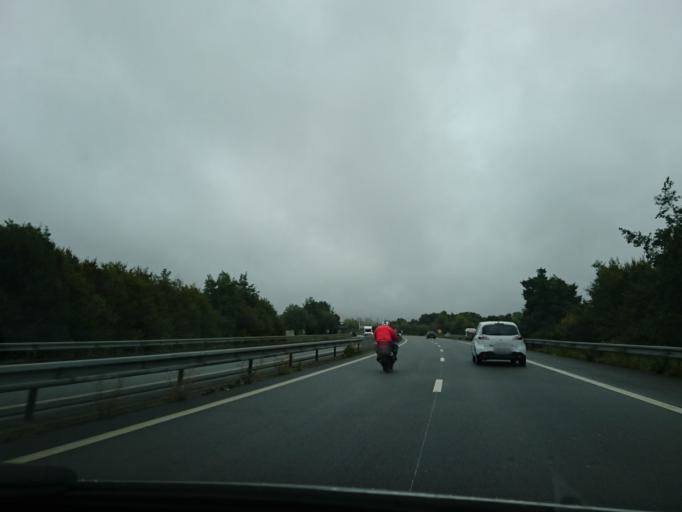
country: FR
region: Brittany
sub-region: Departement du Morbihan
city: Auray
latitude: 47.6631
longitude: -3.0099
